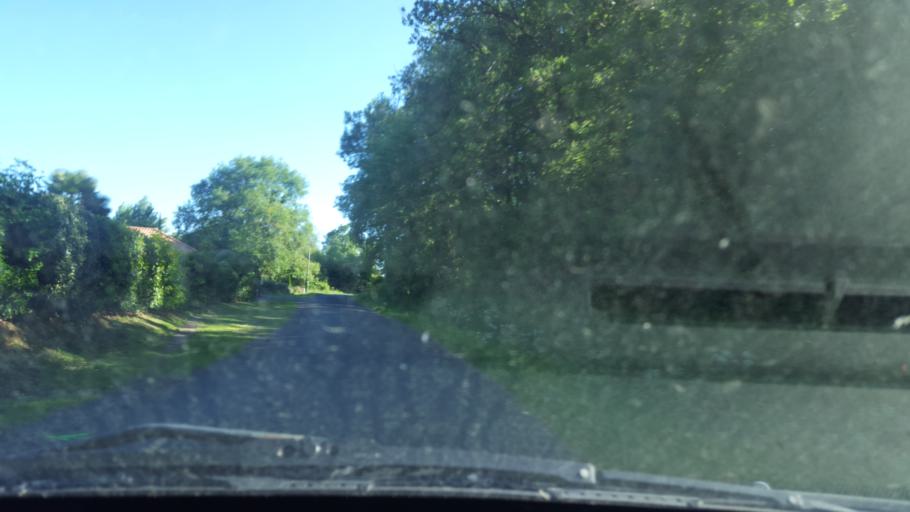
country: FR
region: Pays de la Loire
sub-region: Departement de la Loire-Atlantique
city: Saint-Philbert-de-Grand-Lieu
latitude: 47.0317
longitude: -1.6692
